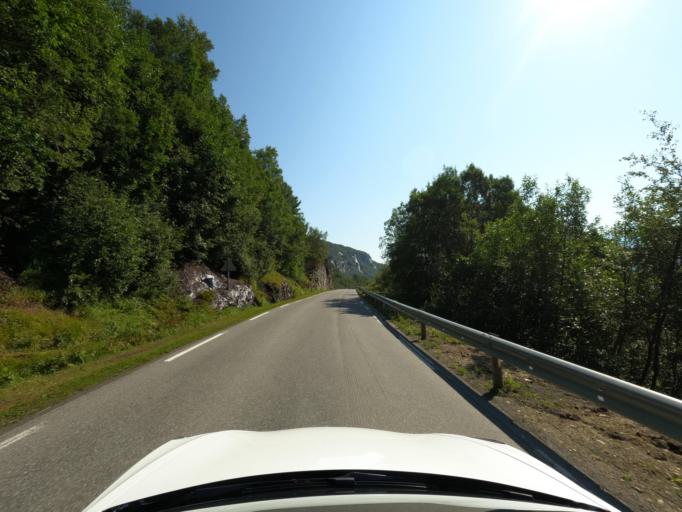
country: NO
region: Nordland
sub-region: Narvik
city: Narvik
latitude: 68.3585
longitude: 17.2687
